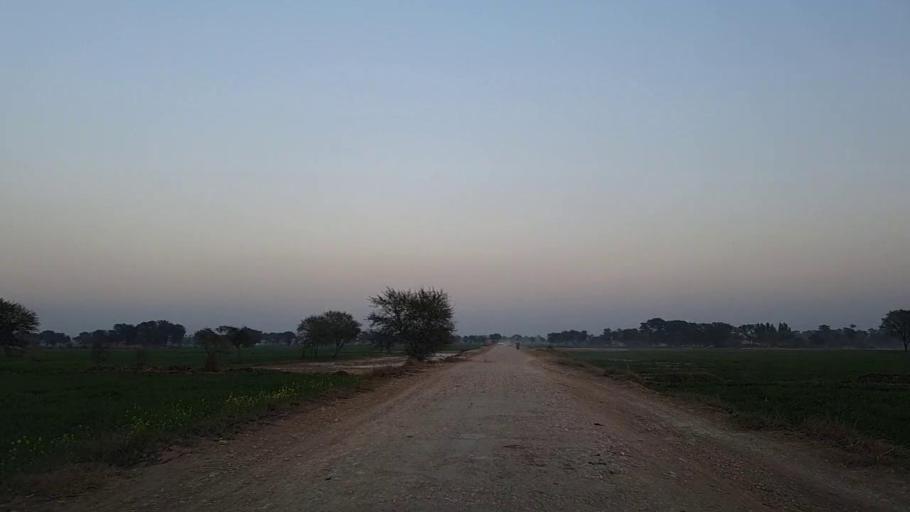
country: PK
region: Sindh
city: Naushahro Firoz
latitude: 26.8005
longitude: 68.0161
